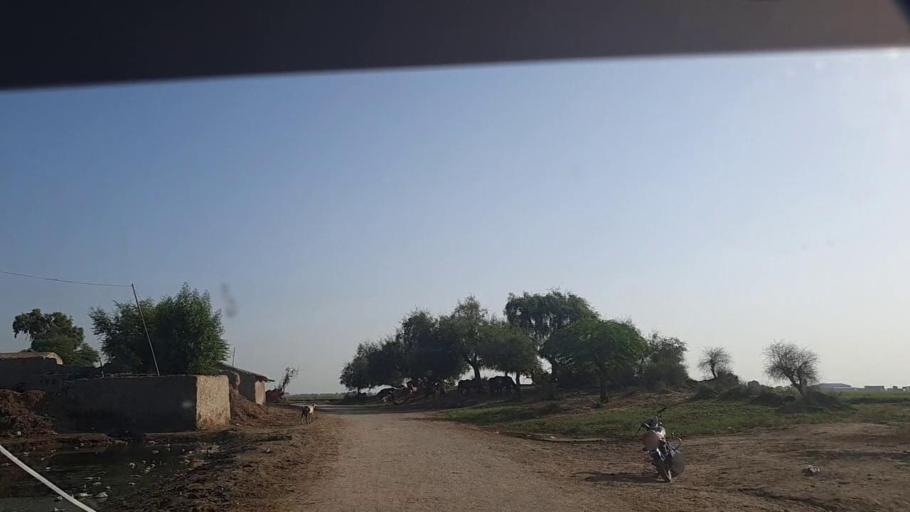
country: PK
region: Sindh
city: Tangwani
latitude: 28.2636
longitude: 69.0140
